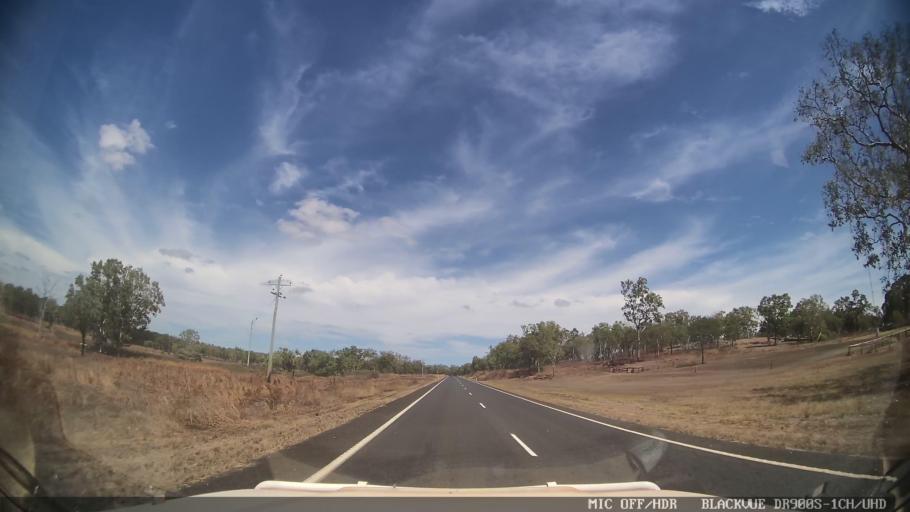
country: AU
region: Queensland
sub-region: Cook
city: Cooktown
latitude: -15.7965
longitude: 144.9264
